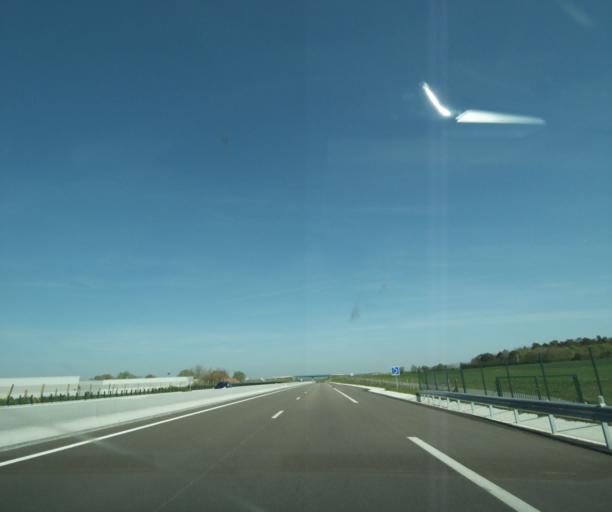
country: FR
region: Bourgogne
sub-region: Departement de la Nievre
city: Saint-Pierre-le-Moutier
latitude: 46.8138
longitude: 3.1232
